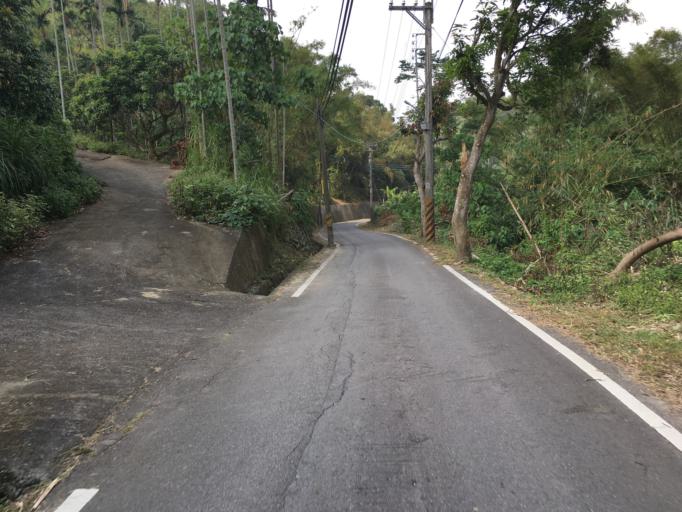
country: TW
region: Taiwan
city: Fengyuan
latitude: 24.1842
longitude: 120.7747
